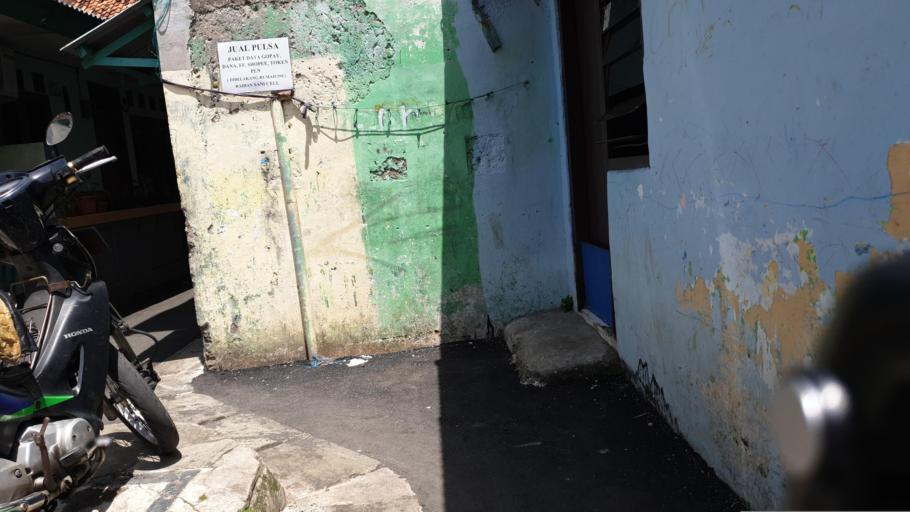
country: ID
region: Jakarta Raya
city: Jakarta
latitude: -6.2496
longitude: 106.7873
